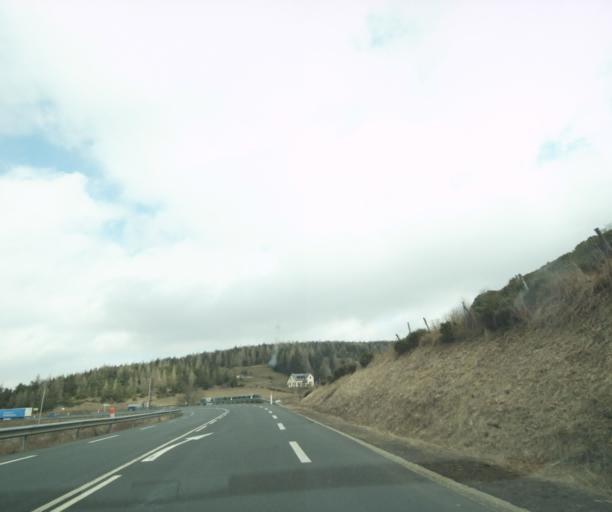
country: FR
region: Languedoc-Roussillon
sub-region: Departement de la Lozere
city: Mende
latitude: 44.6257
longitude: 3.6747
